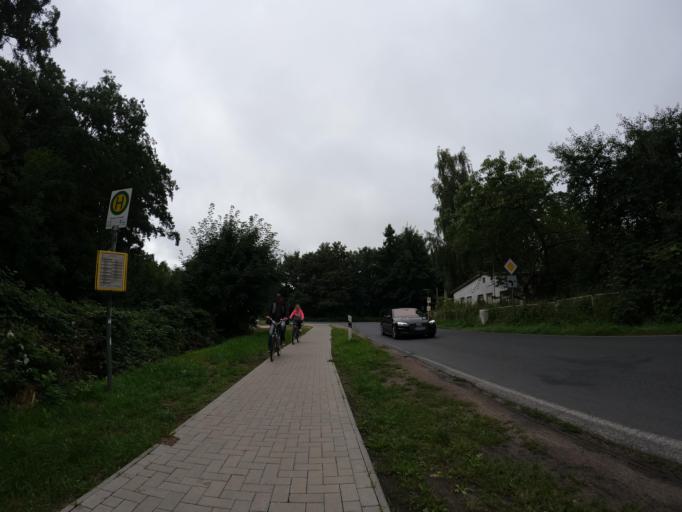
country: DE
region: Mecklenburg-Vorpommern
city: Ostseebad Gohren
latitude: 54.3030
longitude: 13.7021
